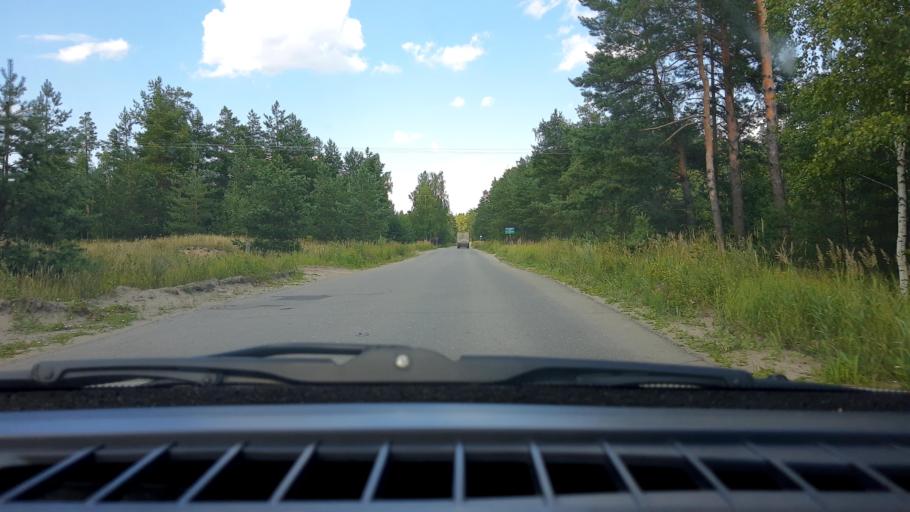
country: RU
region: Nizjnij Novgorod
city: Babino
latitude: 56.3207
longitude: 43.6296
